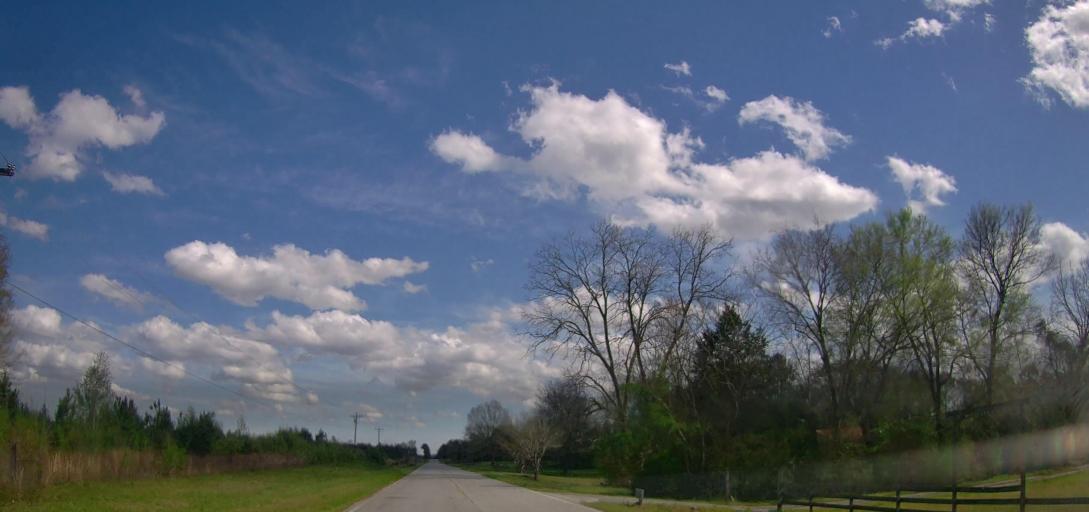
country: US
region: Georgia
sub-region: Wilkinson County
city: Gordon
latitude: 32.8342
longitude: -83.4329
